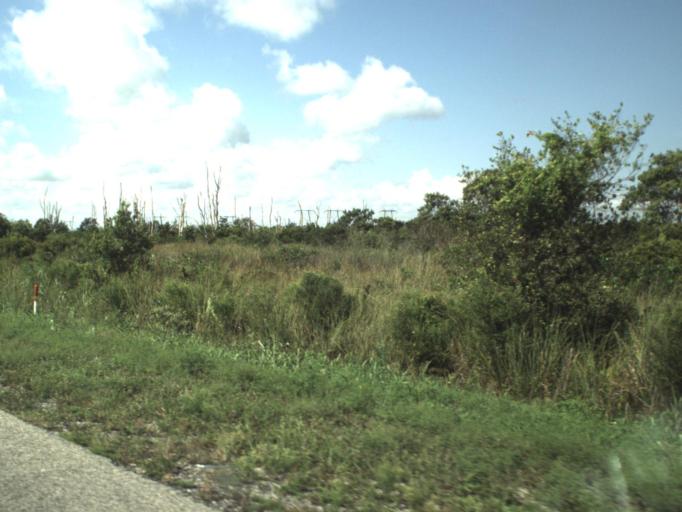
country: US
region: Florida
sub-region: Broward County
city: Weston
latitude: 26.0863
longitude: -80.4344
